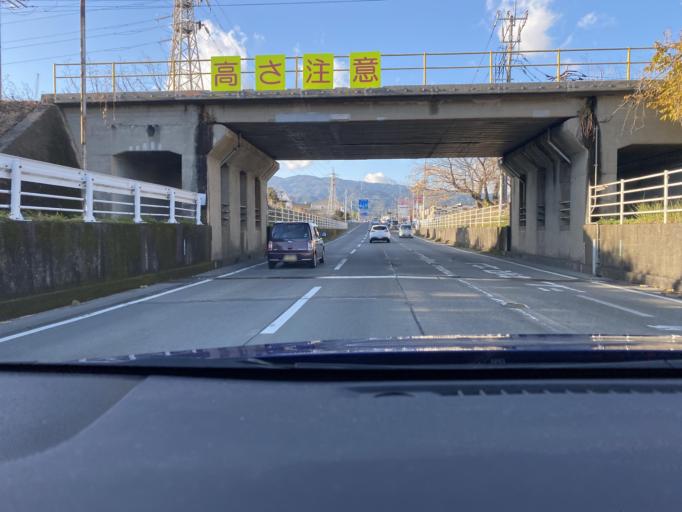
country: JP
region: Saga Prefecture
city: Tosu
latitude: 33.3612
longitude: 130.5053
